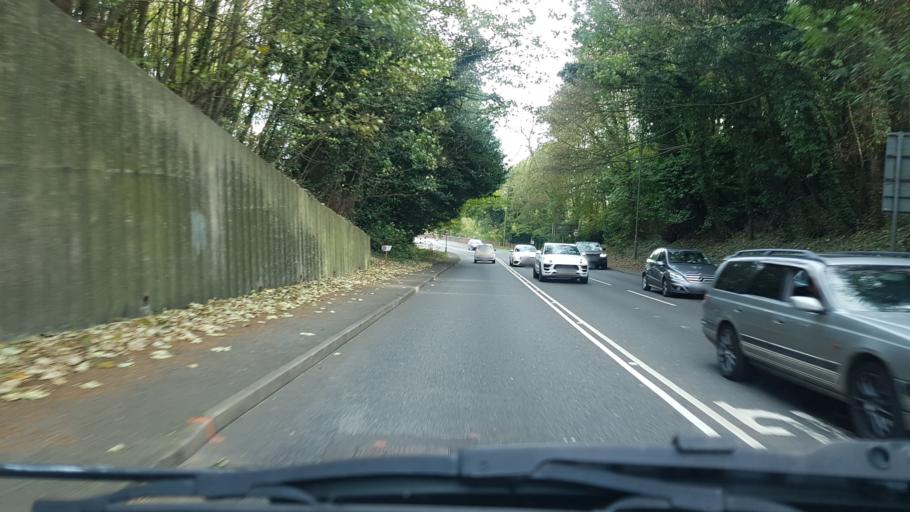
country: GB
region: England
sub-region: Surrey
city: Cobham
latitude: 51.3338
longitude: -0.4261
